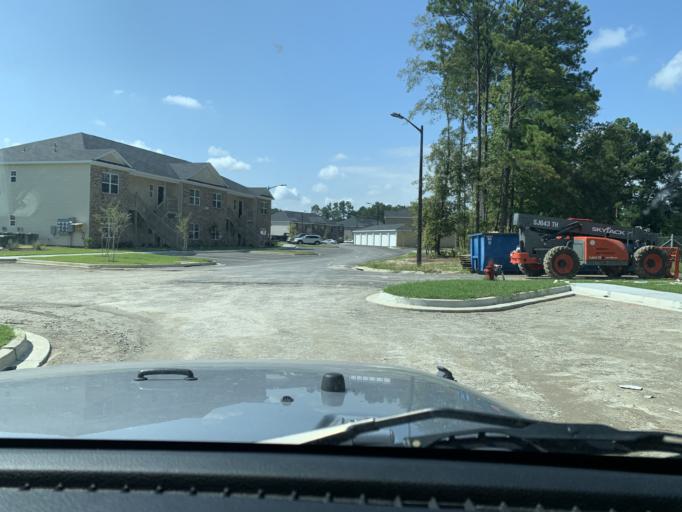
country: US
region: Georgia
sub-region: Chatham County
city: Bloomingdale
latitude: 32.1350
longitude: -81.2912
